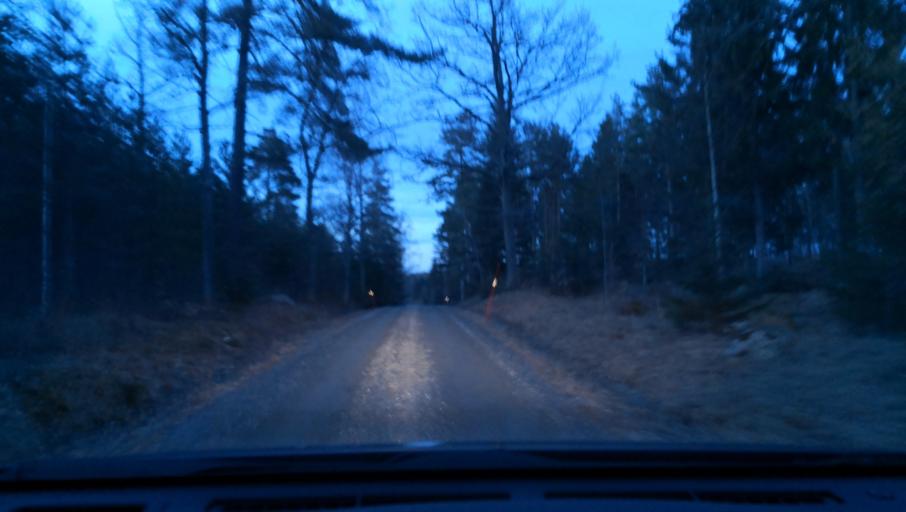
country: SE
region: Uppsala
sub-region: Enkopings Kommun
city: Dalby
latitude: 59.5645
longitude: 17.3737
